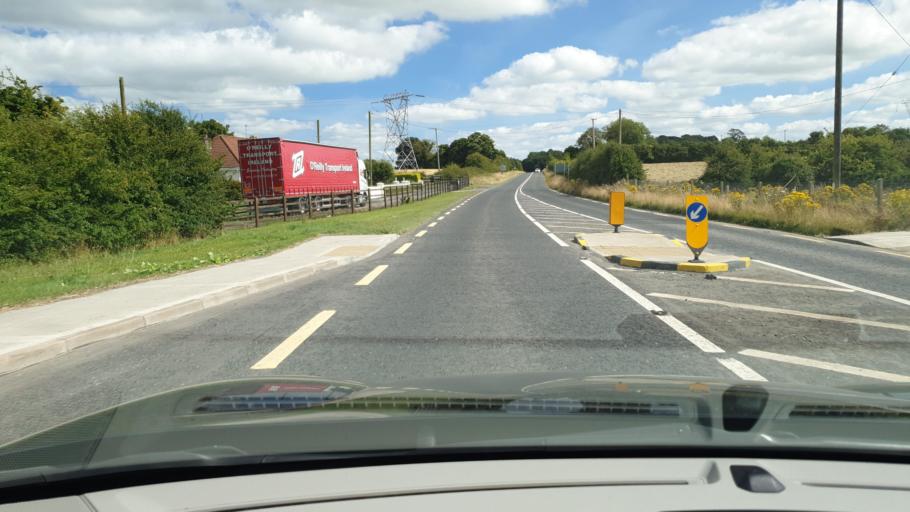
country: IE
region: Leinster
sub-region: An Mhi
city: Dunshaughlin
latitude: 53.5214
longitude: -6.6495
